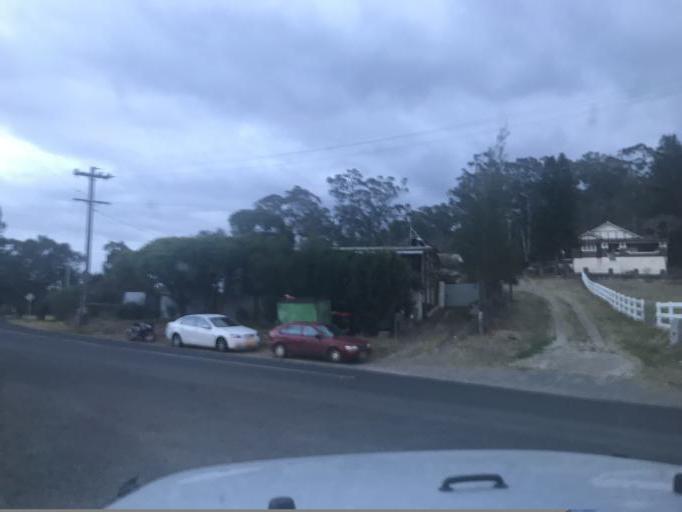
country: AU
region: New South Wales
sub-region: Hawkesbury
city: Pitt Town
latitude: -33.5028
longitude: 150.8761
